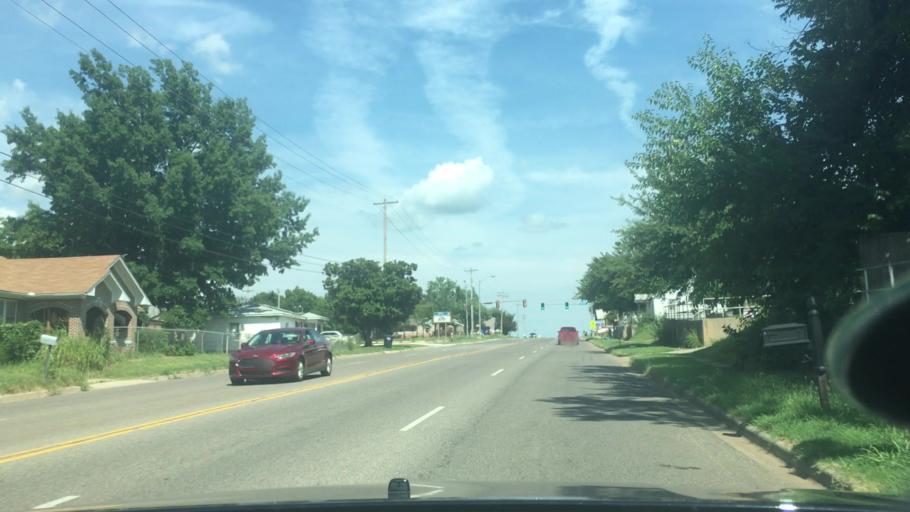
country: US
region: Oklahoma
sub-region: Pottawatomie County
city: Shawnee
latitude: 35.3327
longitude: -96.9073
